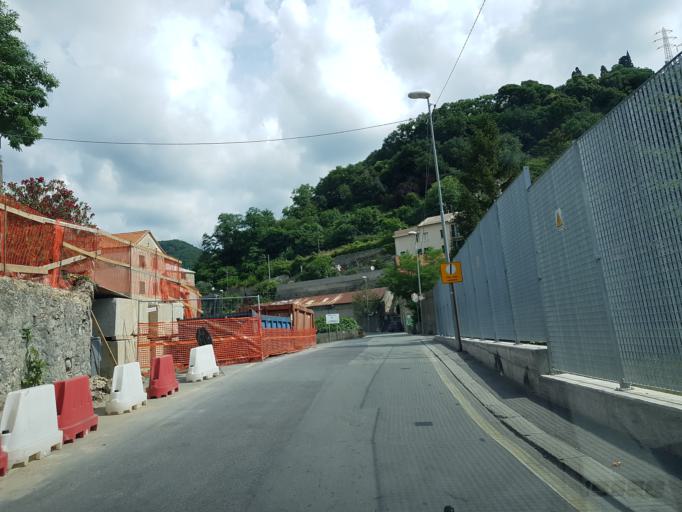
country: IT
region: Liguria
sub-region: Provincia di Genova
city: San Teodoro
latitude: 44.4373
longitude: 8.8548
